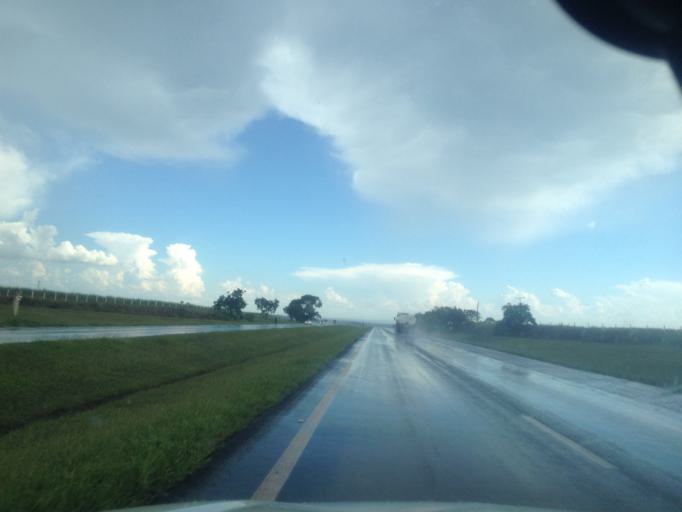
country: BR
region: Sao Paulo
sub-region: Orlandia
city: Orlandia
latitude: -20.7527
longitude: -47.8930
